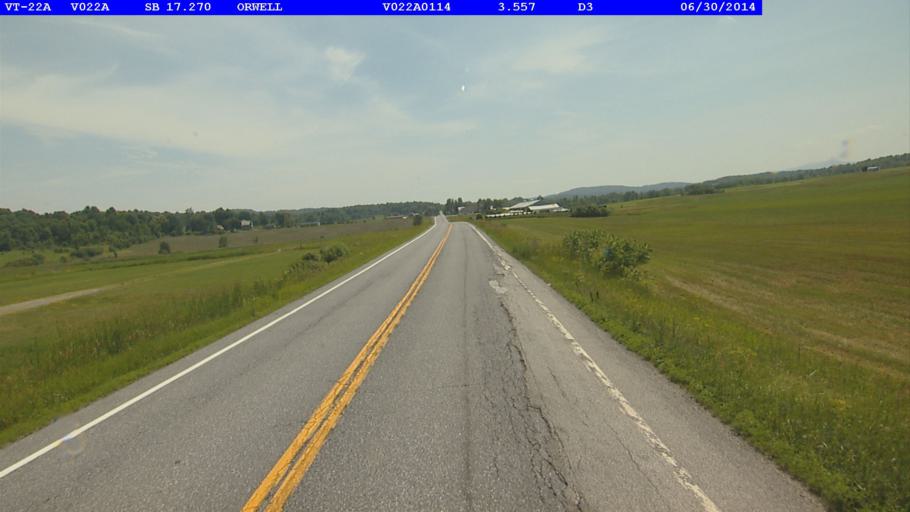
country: US
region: New York
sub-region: Essex County
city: Ticonderoga
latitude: 43.8082
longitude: -73.3044
